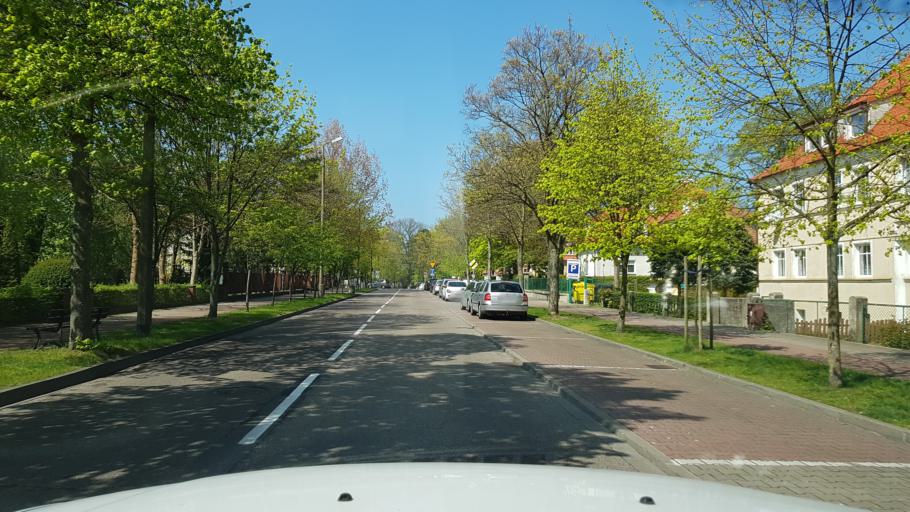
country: PL
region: Pomeranian Voivodeship
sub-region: Powiat slupski
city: Ustka
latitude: 54.5860
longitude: 16.8645
